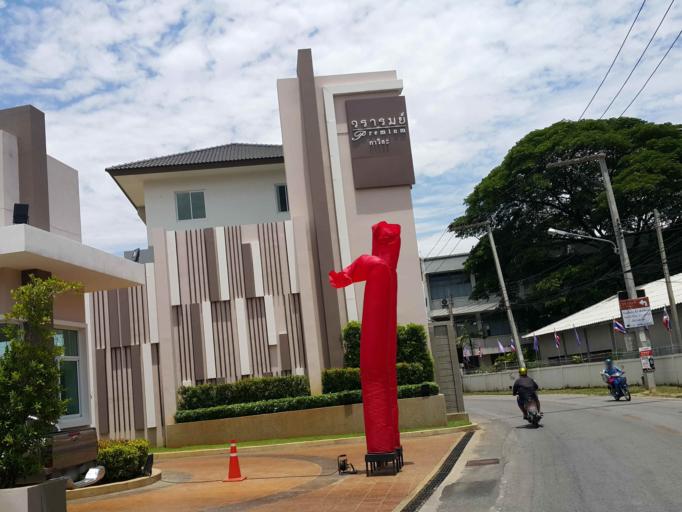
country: TH
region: Chiang Mai
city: Chiang Mai
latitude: 18.7823
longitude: 99.0137
